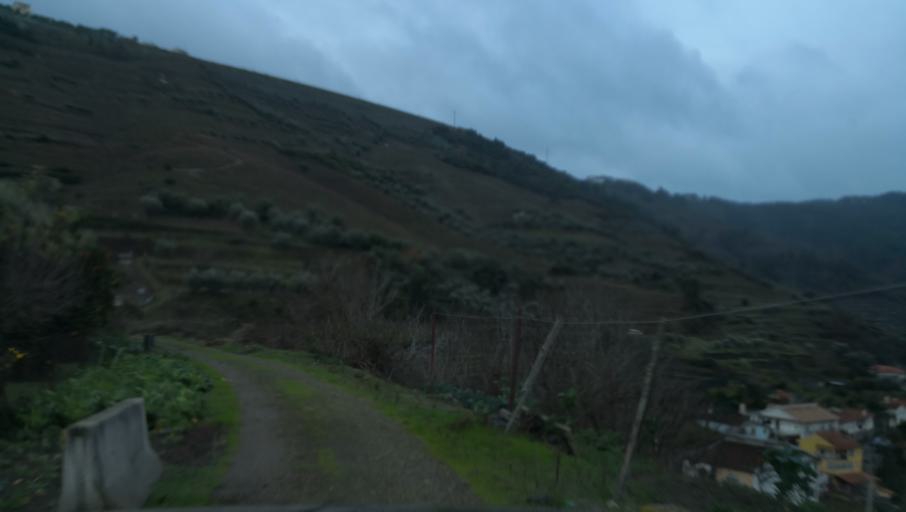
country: PT
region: Vila Real
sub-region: Vila Real
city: Vila Real
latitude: 41.2357
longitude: -7.7398
